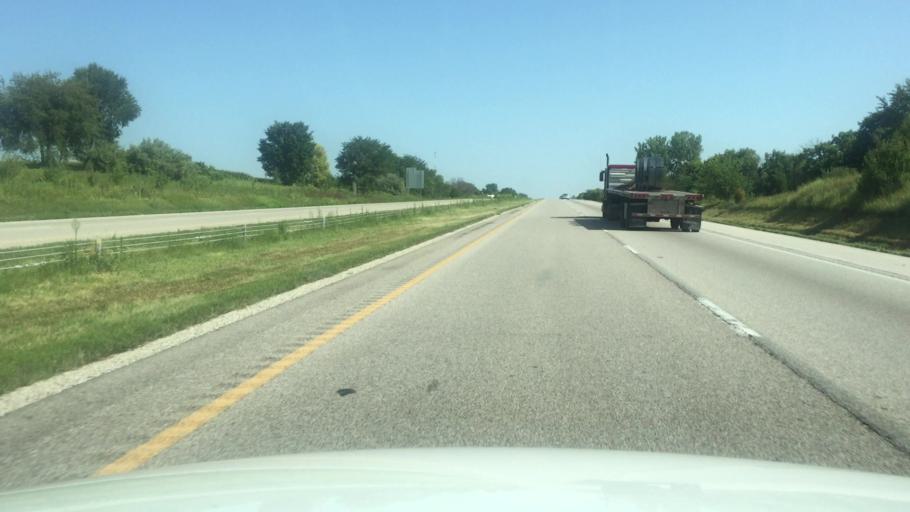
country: US
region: Missouri
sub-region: Platte County
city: Platte City
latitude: 39.3989
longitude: -94.7895
